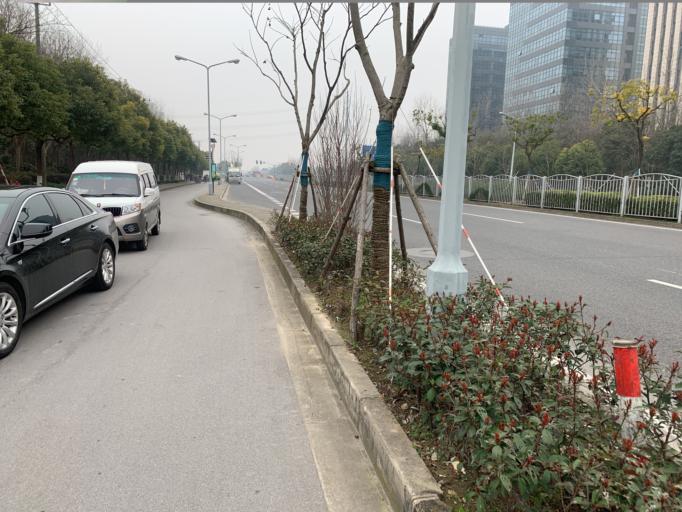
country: CN
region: Shanghai Shi
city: Huamu
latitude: 31.2462
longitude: 121.6212
